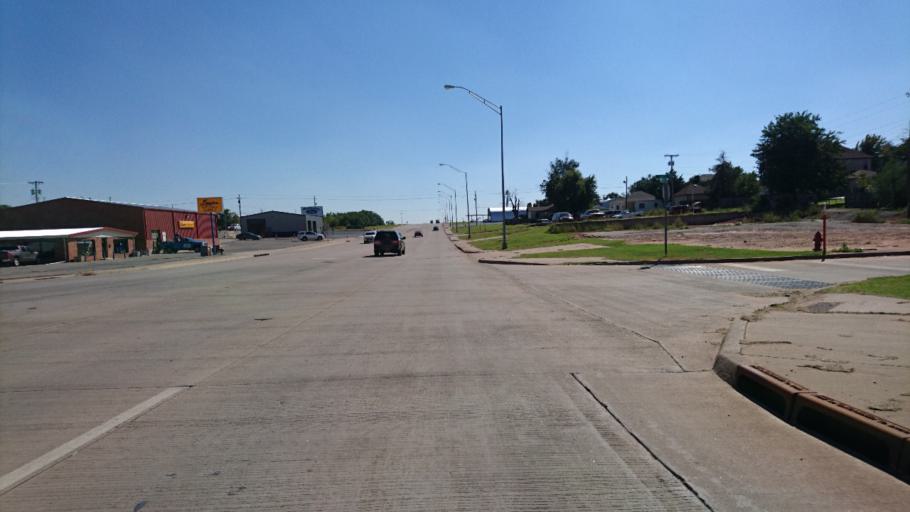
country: US
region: Oklahoma
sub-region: Custer County
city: Clinton
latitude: 35.5105
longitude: -98.9649
